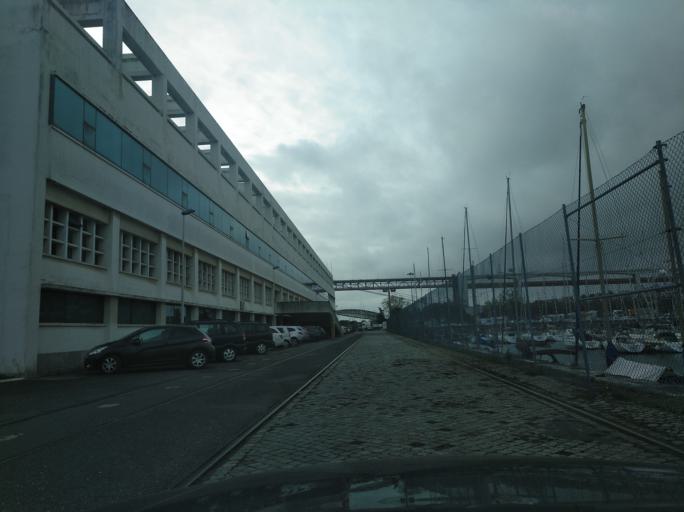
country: PT
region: Setubal
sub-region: Almada
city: Almada
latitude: 38.7005
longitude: -9.1706
